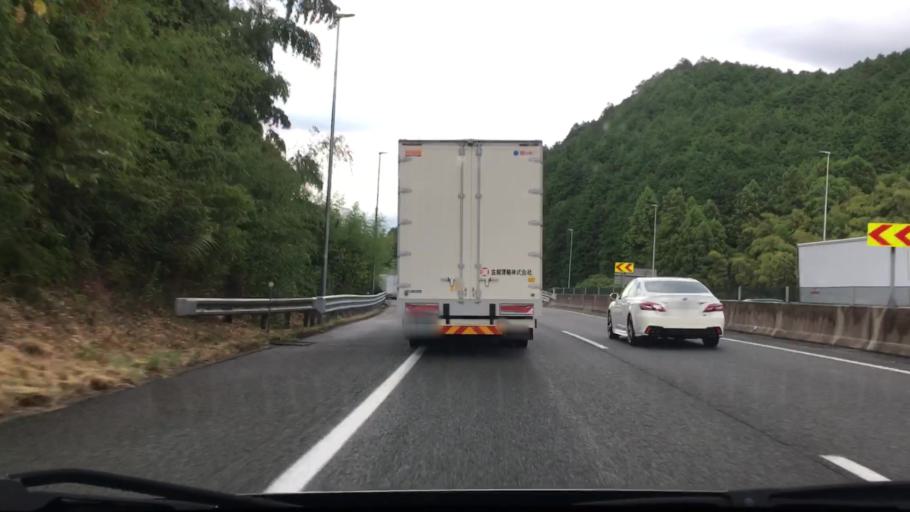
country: JP
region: Fukuoka
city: Nishifukuma
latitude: 33.7492
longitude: 130.5581
